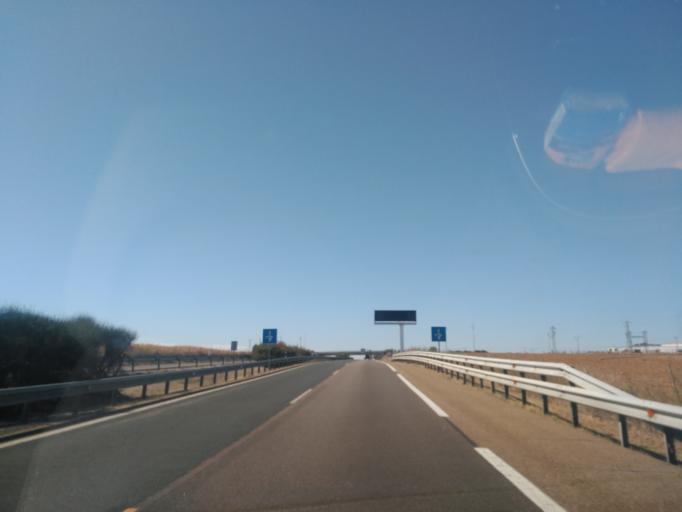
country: ES
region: Castille and Leon
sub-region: Provincia de Valladolid
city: Geria
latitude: 41.5628
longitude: -4.8654
